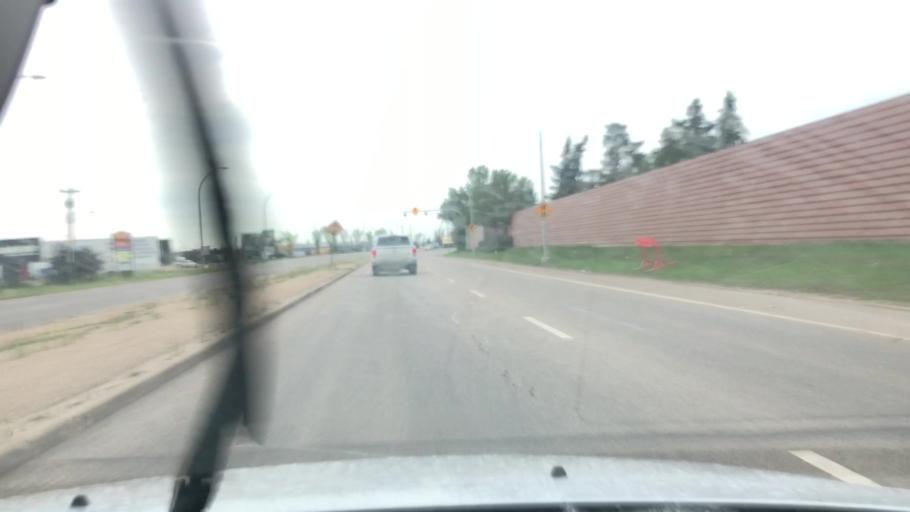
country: CA
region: Alberta
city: St. Albert
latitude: 53.5565
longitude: -113.6047
